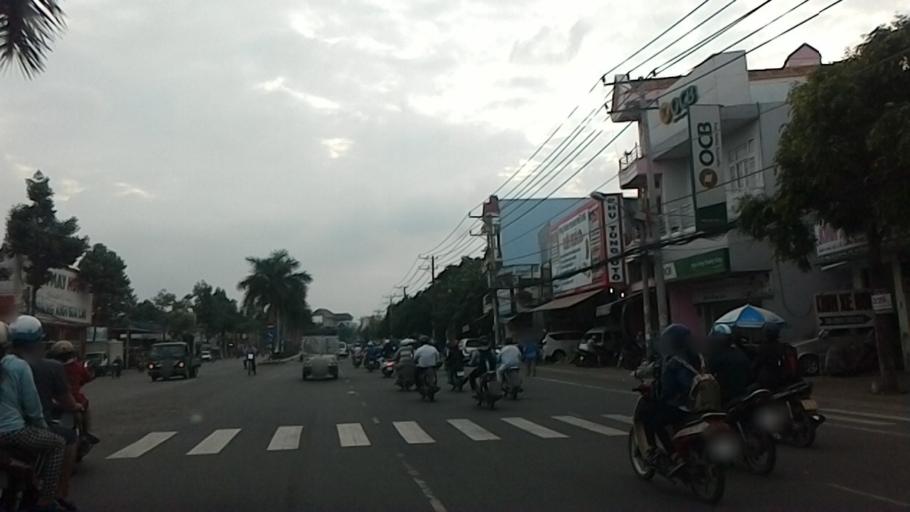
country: VN
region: Can Tho
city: Cai Rang
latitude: 10.0165
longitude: 105.7605
